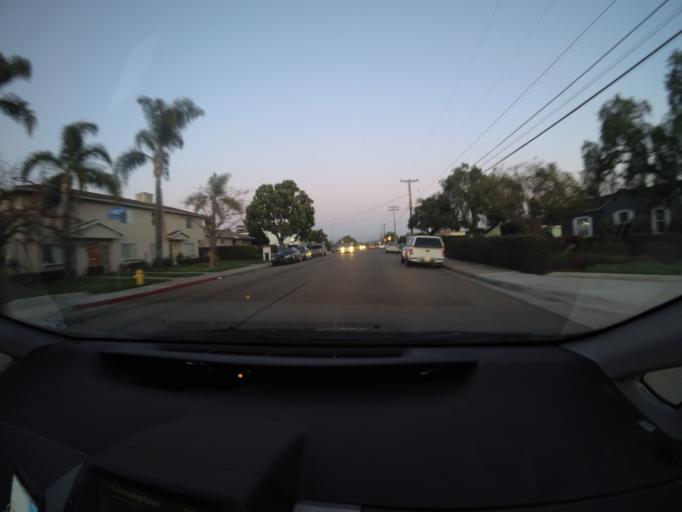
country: US
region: California
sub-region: San Diego County
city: Imperial Beach
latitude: 32.5807
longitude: -117.1071
